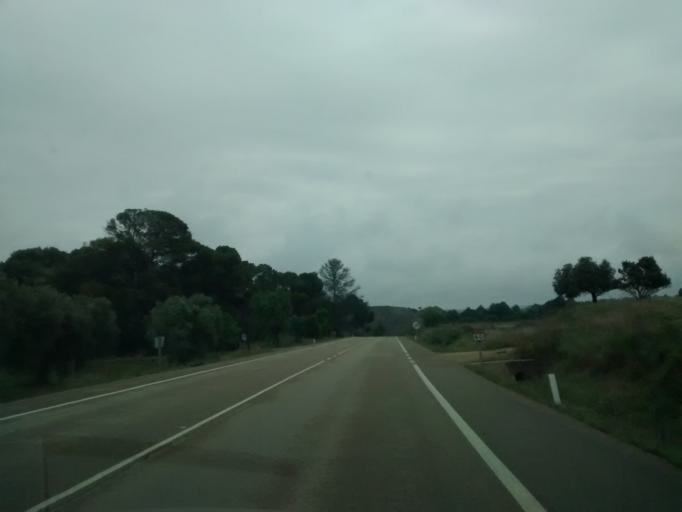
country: ES
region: Aragon
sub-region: Provincia de Zaragoza
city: Caspe
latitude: 41.2136
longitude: 0.0063
